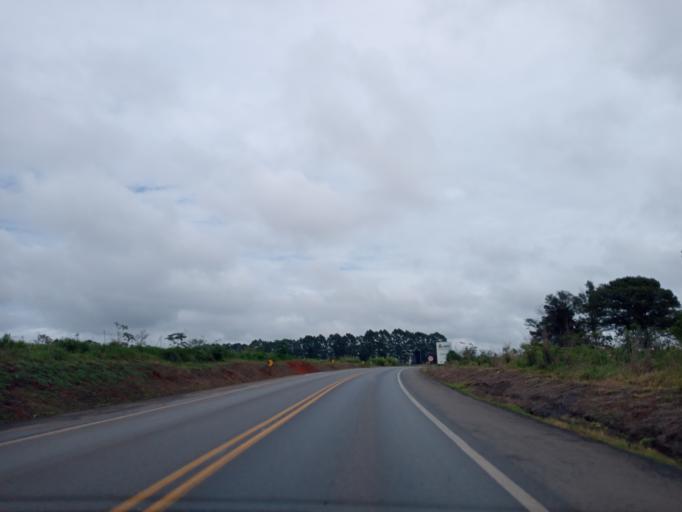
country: BR
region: Minas Gerais
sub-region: Campos Altos
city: Campos Altos
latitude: -19.6604
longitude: -46.2048
